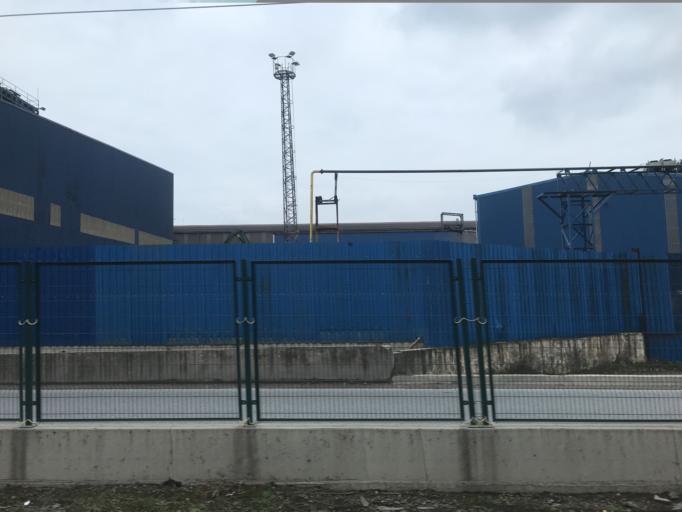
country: TR
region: Kocaeli
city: Darica
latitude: 40.8033
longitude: 29.3737
